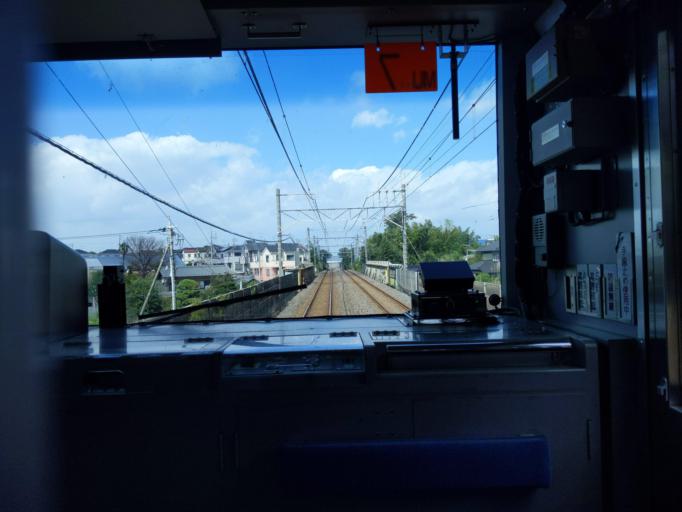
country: JP
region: Chiba
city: Funabashi
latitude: 35.7383
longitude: 139.9622
